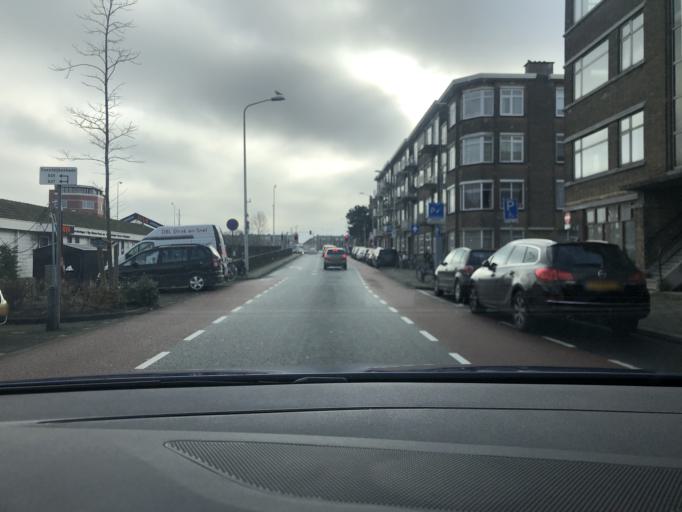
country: NL
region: South Holland
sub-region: Gemeente Den Haag
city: The Hague
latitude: 52.0641
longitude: 4.2719
